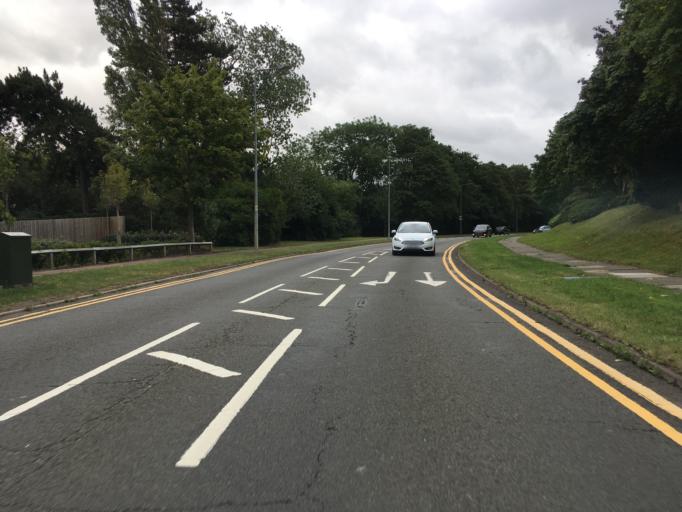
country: GB
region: England
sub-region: Buckinghamshire
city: Bletchley
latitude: 52.0022
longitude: -0.7397
